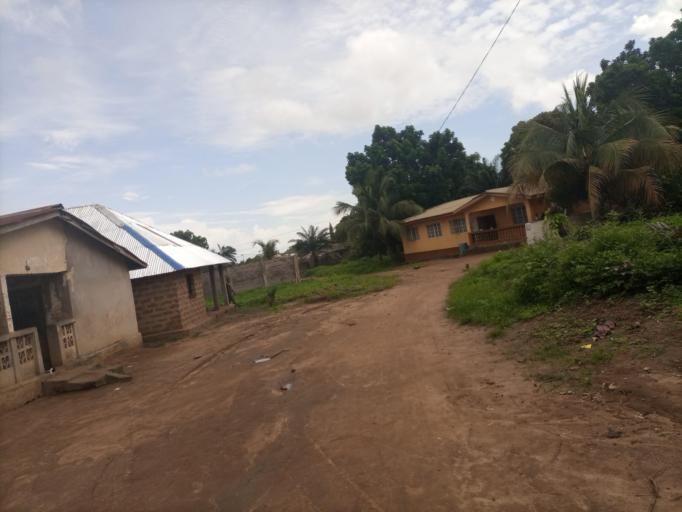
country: SL
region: Northern Province
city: Masoyila
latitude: 8.5928
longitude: -13.1649
